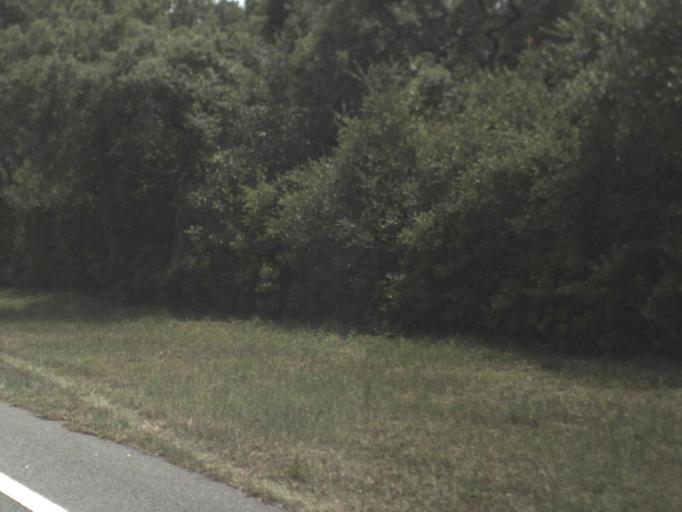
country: US
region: Florida
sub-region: Duval County
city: Atlantic Beach
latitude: 30.4942
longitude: -81.4443
